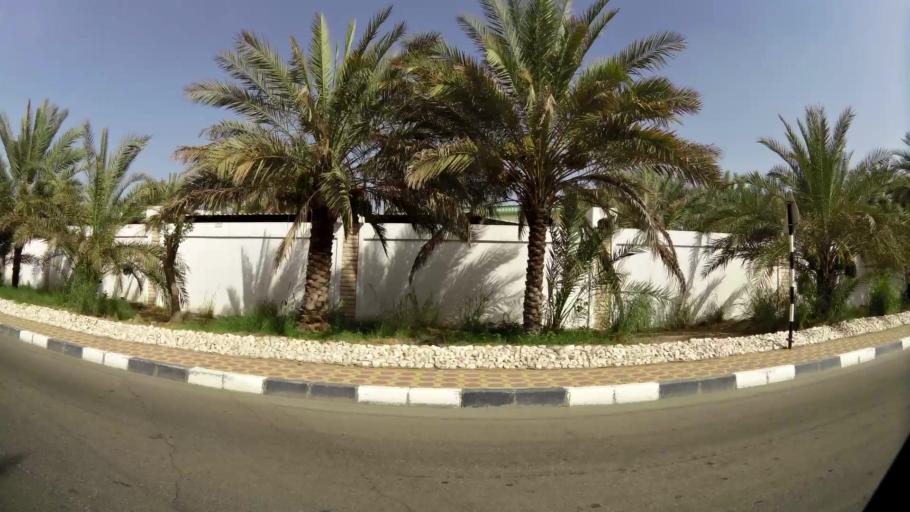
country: AE
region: Abu Dhabi
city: Al Ain
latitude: 24.2448
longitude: 55.6838
